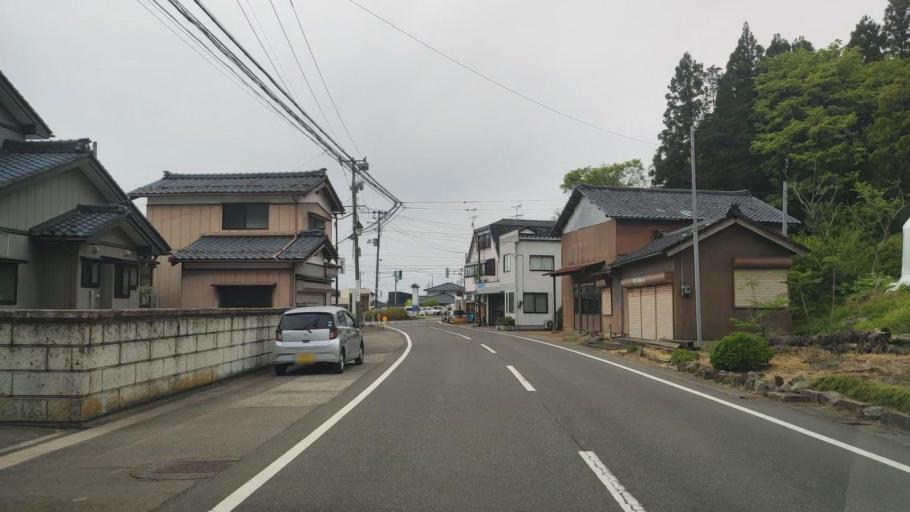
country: JP
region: Niigata
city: Kamo
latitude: 37.7127
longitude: 139.0746
